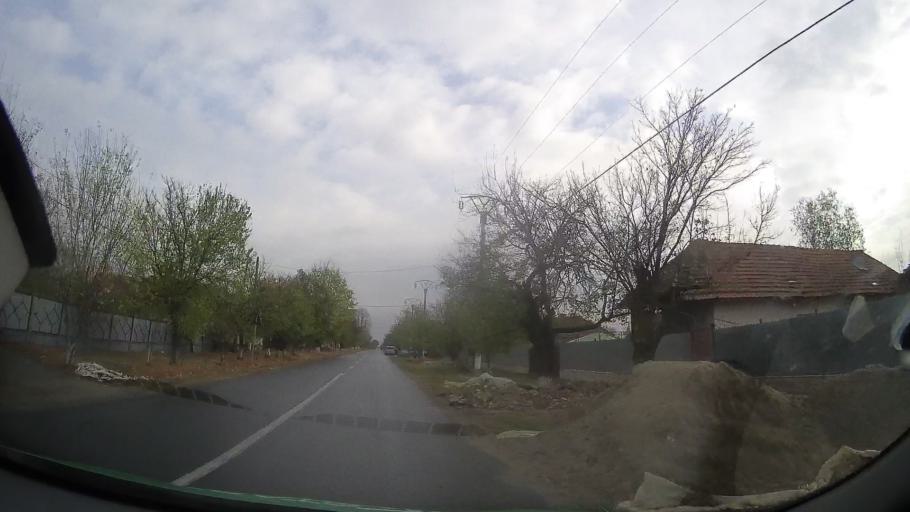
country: RO
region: Ialomita
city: Brazii
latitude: 44.7607
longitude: 26.3622
